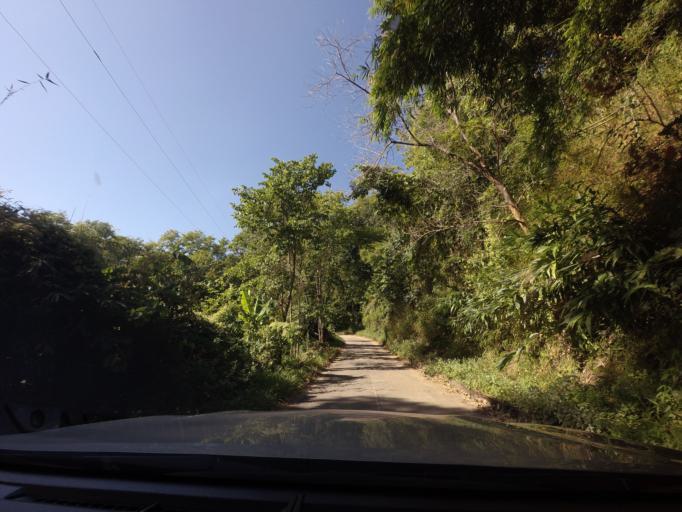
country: TH
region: Lampang
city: Mueang Pan
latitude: 18.8289
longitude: 99.3978
